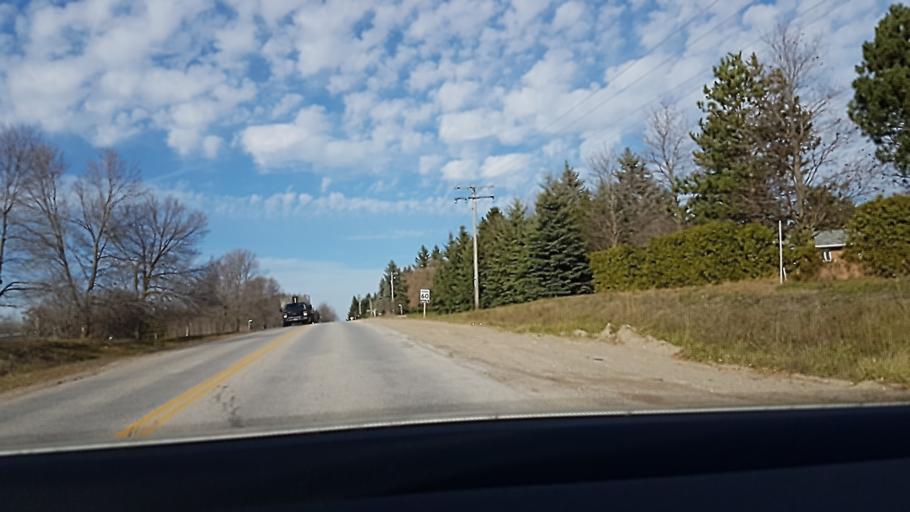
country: CA
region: Ontario
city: Bradford West Gwillimbury
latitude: 44.0424
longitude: -79.7726
